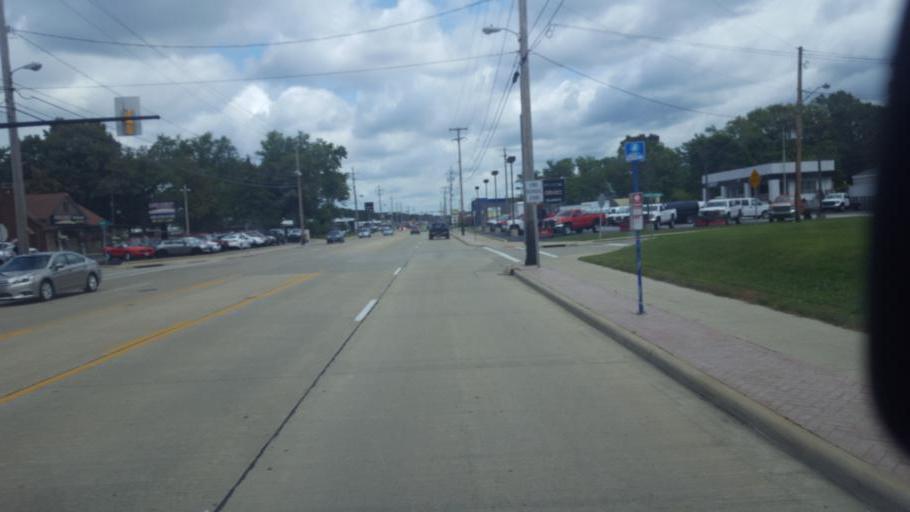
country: US
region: Ohio
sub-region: Lake County
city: Painesville
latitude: 41.6947
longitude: -81.2829
